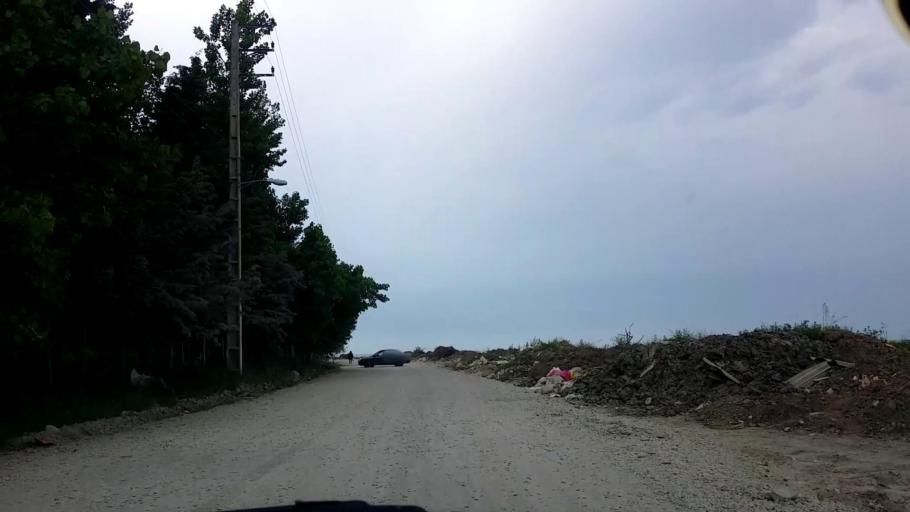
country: IR
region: Mazandaran
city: Chalus
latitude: 36.6827
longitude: 51.4341
